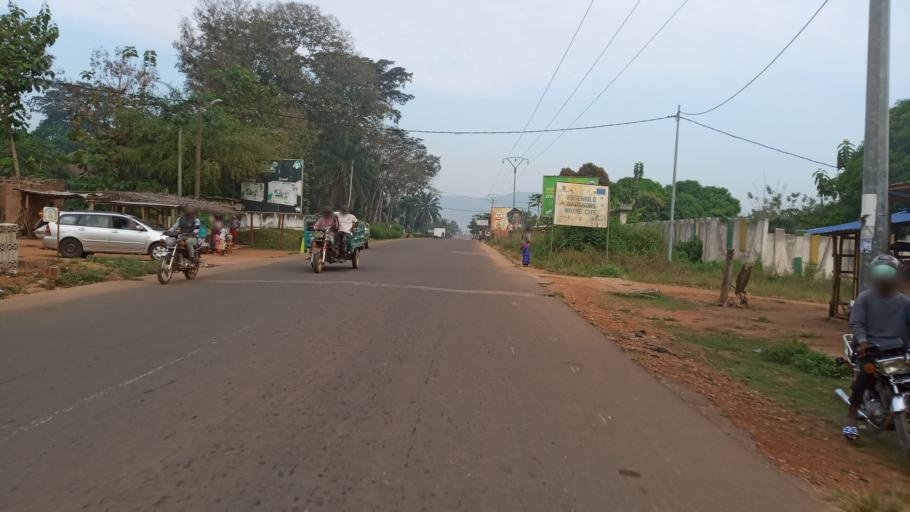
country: TG
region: Plateaux
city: Kpalime
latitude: 6.8910
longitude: 0.6414
